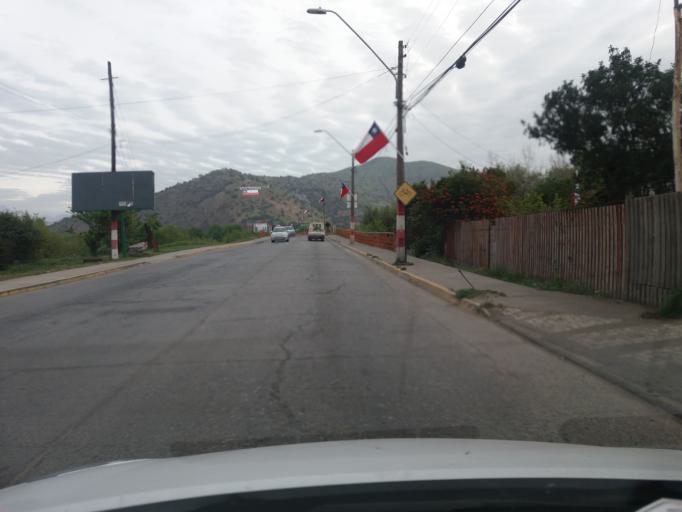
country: CL
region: Valparaiso
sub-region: Provincia de Quillota
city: Hacienda La Calera
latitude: -32.7780
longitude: -71.1915
